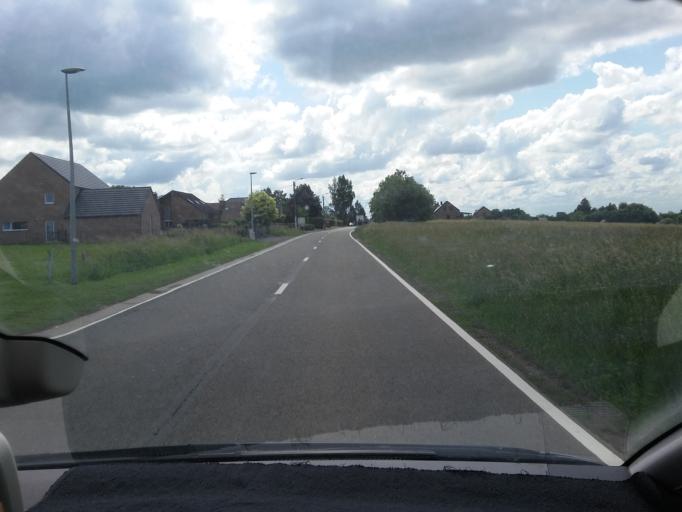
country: BE
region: Wallonia
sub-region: Province de Namur
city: Hamois
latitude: 50.2819
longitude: 5.1767
